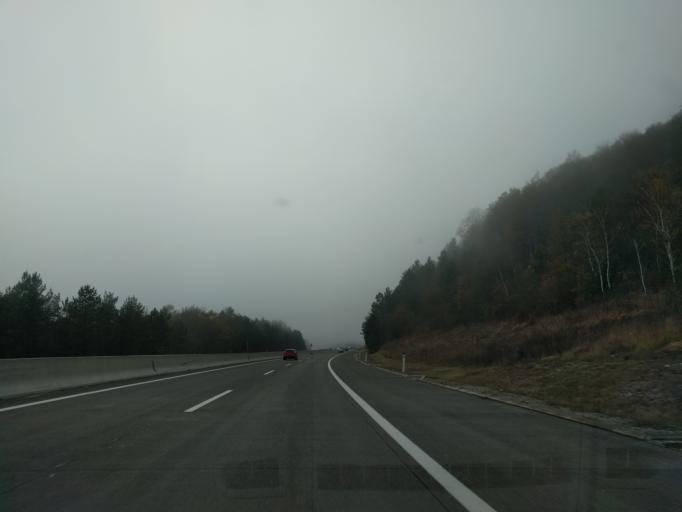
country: AT
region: Lower Austria
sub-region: Politischer Bezirk Wien-Umgebung
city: Wolfsgraben
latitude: 48.1737
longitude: 16.1297
